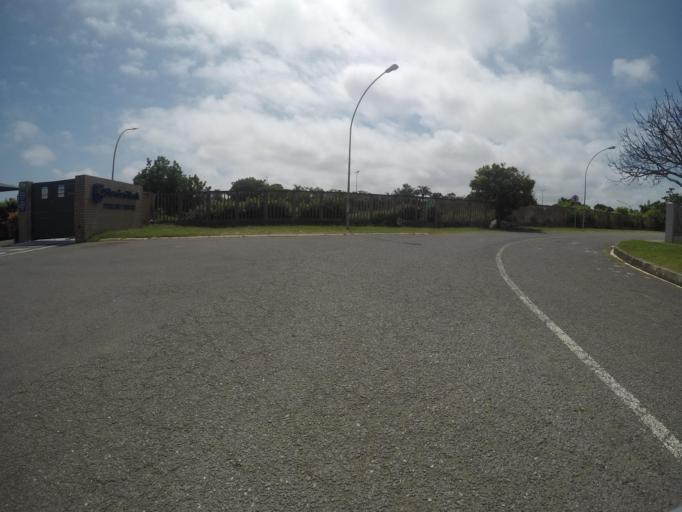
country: ZA
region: Eastern Cape
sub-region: Buffalo City Metropolitan Municipality
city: East London
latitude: -32.9925
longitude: 27.9190
